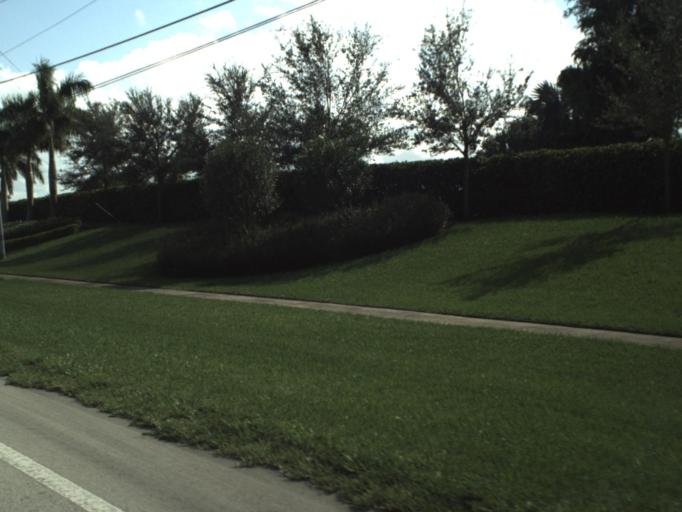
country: US
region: Florida
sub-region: Palm Beach County
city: Villages of Oriole
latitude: 26.4158
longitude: -80.2042
